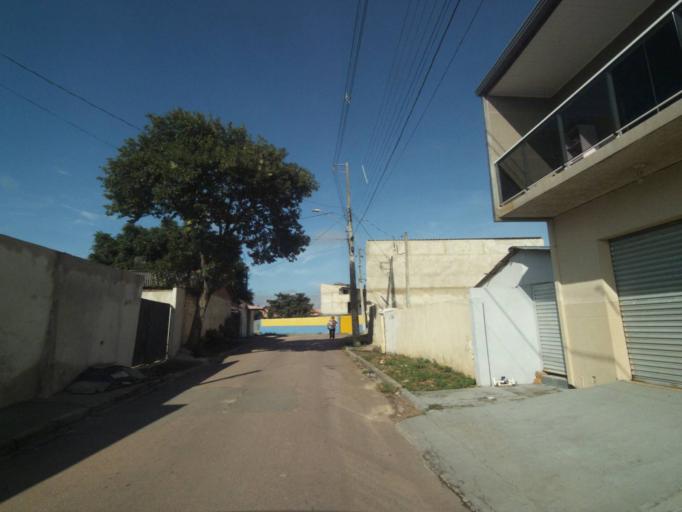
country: BR
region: Parana
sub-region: Pinhais
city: Pinhais
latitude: -25.4706
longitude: -49.1890
